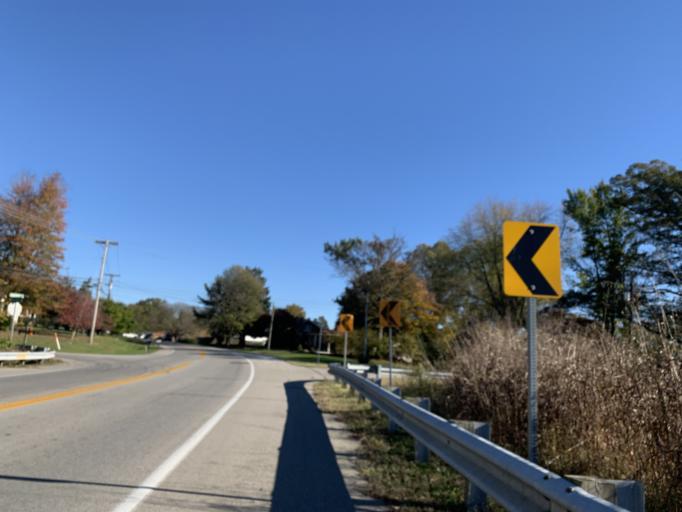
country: US
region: Kentucky
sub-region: Jefferson County
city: Pleasure Ridge Park
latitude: 38.1453
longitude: -85.8833
